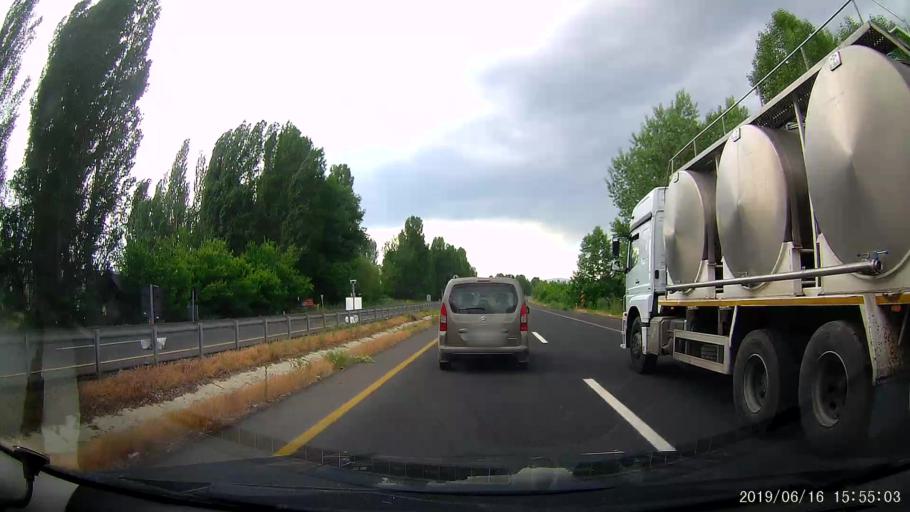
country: TR
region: Erzurum
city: Pasinler
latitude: 39.9778
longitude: 41.6269
